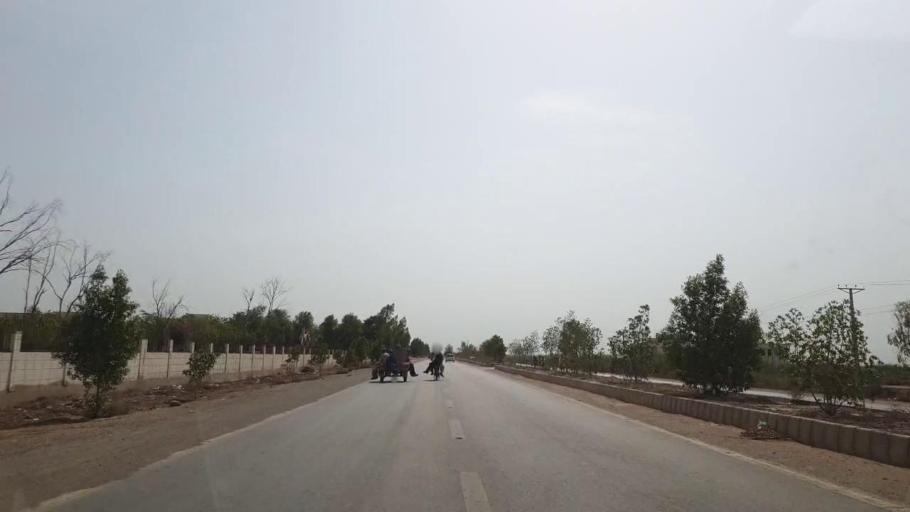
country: PK
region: Sindh
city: Nawabshah
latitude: 26.2334
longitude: 68.3801
